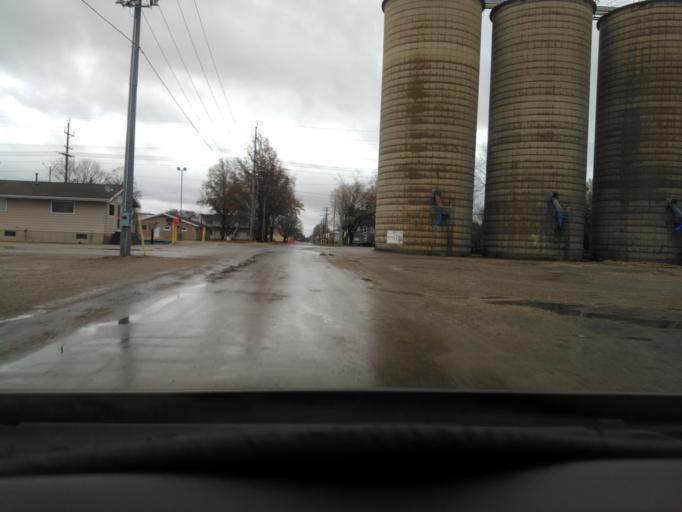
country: US
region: Illinois
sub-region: Effingham County
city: Altamont
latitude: 39.0596
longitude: -88.7524
